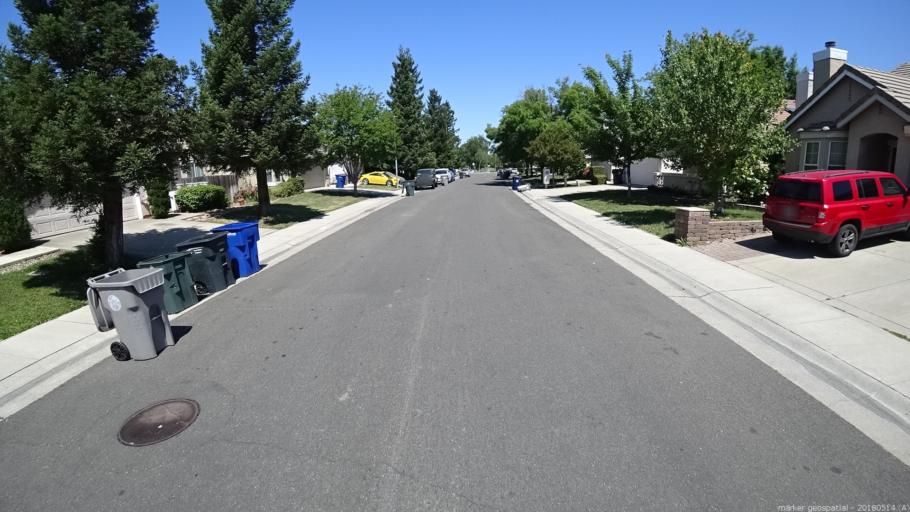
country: US
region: California
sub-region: Yolo County
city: West Sacramento
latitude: 38.6358
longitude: -121.5305
